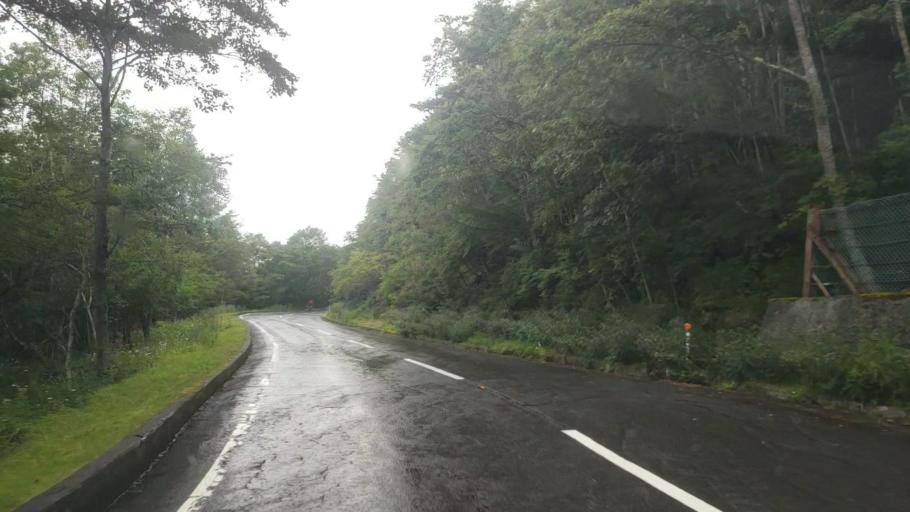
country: JP
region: Shizuoka
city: Fujinomiya
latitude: 35.3291
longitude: 138.7290
